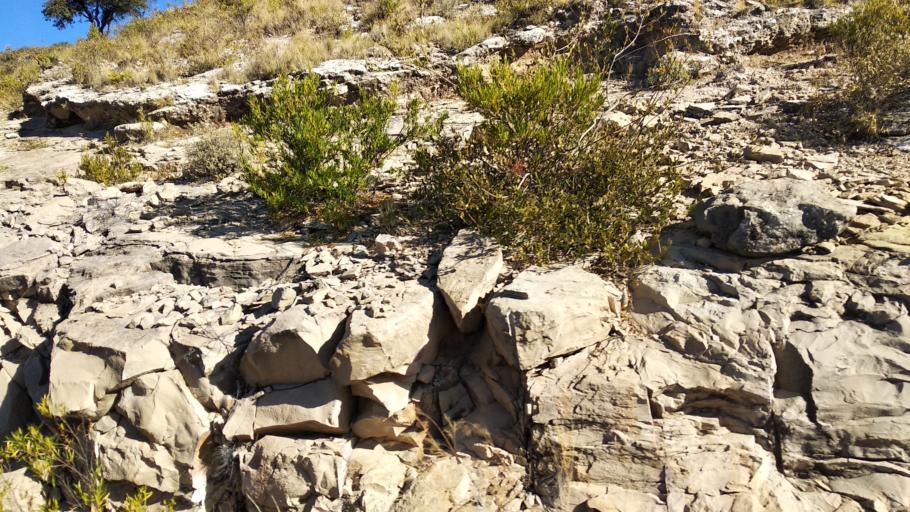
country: BO
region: Cochabamba
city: Mizque
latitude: -18.1026
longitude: -65.7640
